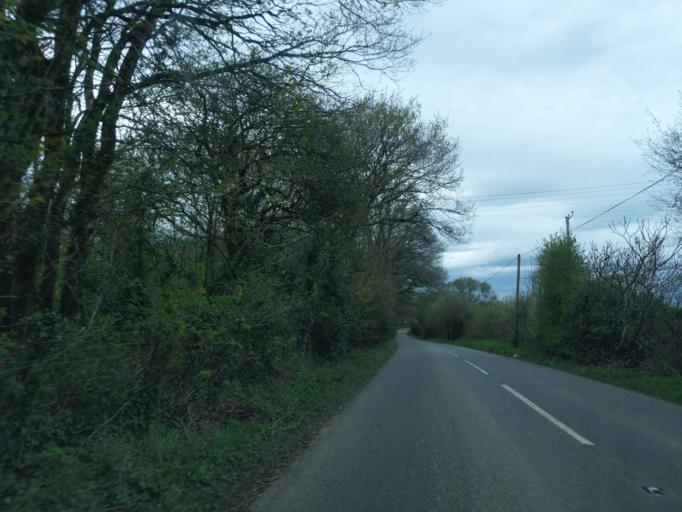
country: GB
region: England
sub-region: Devon
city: Winkleigh
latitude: 50.8702
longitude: -3.9672
